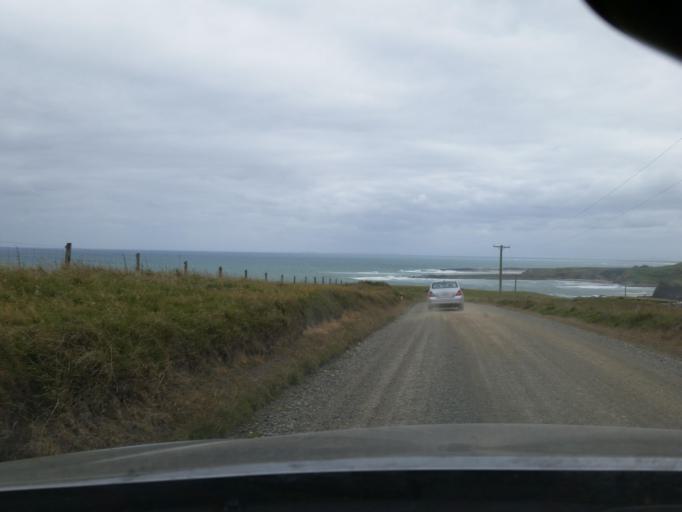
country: NZ
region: Otago
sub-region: Clutha District
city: Papatowai
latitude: -46.6688
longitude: 169.0050
